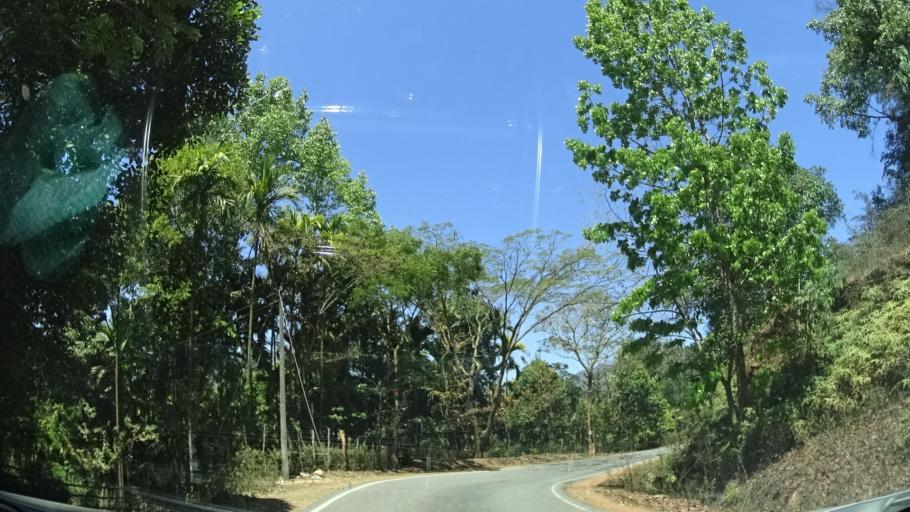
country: IN
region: Karnataka
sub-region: Chikmagalur
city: Sringeri
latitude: 13.2260
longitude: 75.3529
